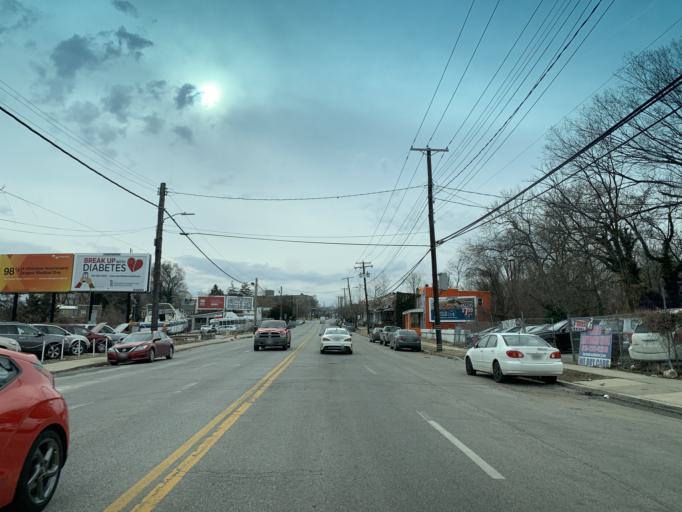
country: US
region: Maryland
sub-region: Baltimore County
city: Lansdowne
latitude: 39.2762
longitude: -76.6652
